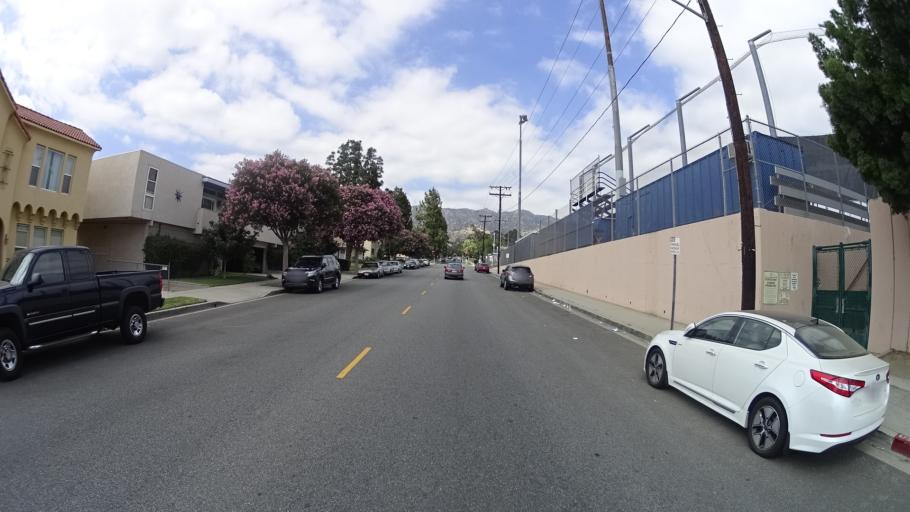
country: US
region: California
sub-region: Los Angeles County
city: Burbank
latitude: 34.1895
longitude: -118.3170
